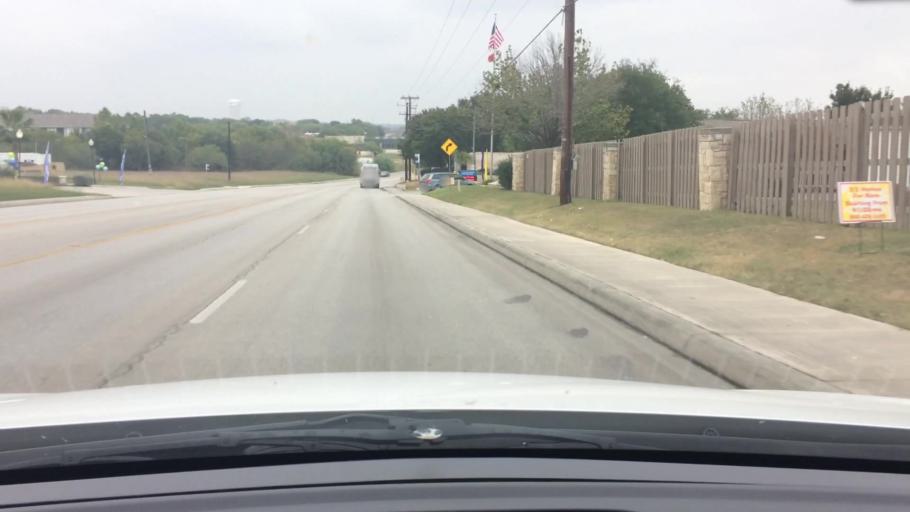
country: US
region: Texas
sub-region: Bexar County
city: Converse
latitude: 29.5242
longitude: -98.3430
